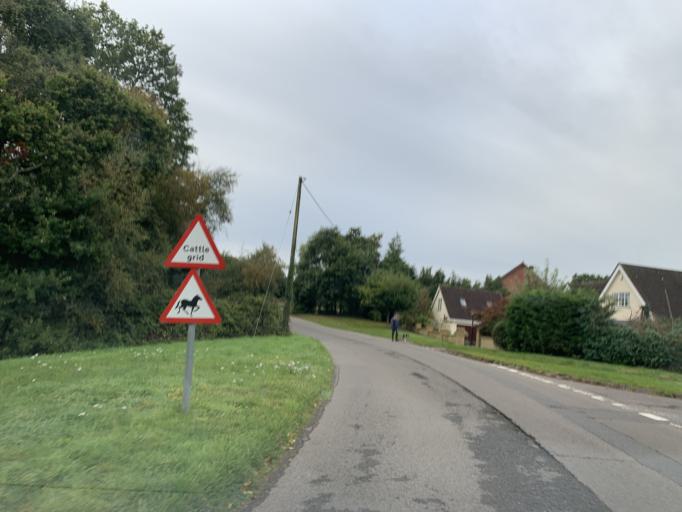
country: GB
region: England
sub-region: Wiltshire
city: Whiteparish
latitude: 50.9594
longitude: -1.6346
